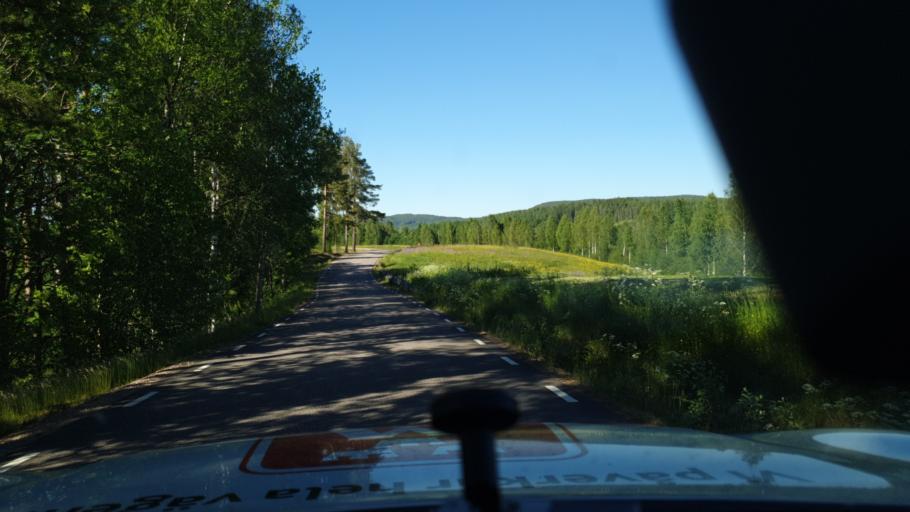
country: SE
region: Vaermland
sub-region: Torsby Kommun
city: Torsby
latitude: 60.1831
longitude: 13.0383
